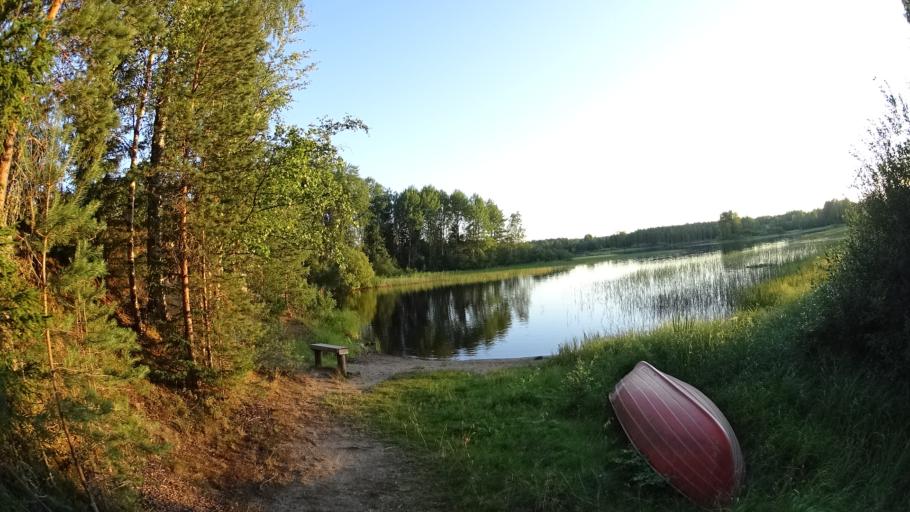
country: FI
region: Central Finland
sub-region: Jyvaeskylae
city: Petaejaevesi
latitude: 62.2536
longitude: 25.1789
